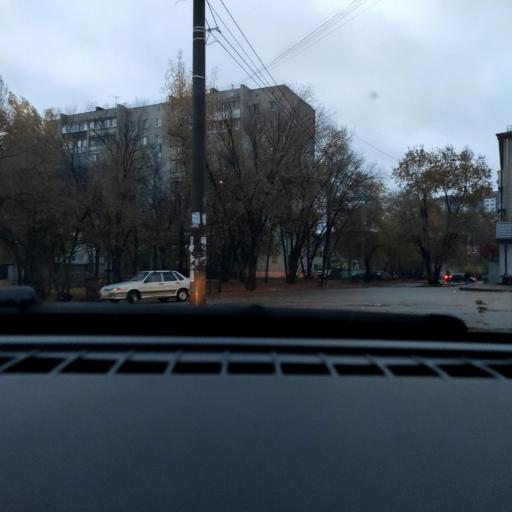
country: RU
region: Voronezj
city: Voronezh
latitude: 51.7193
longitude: 39.2654
